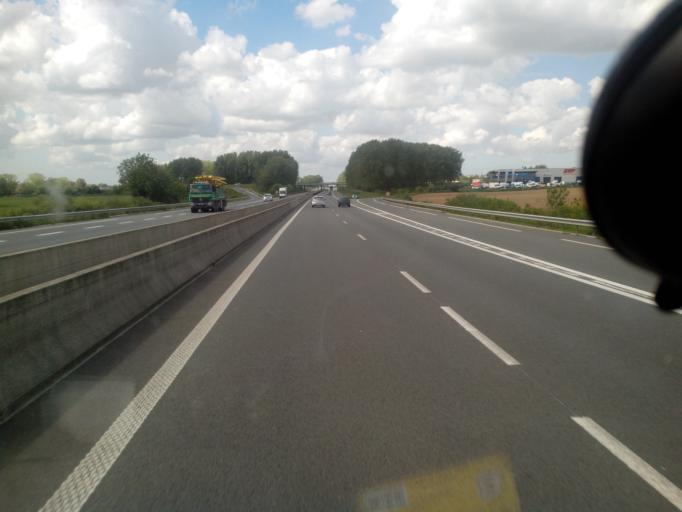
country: FR
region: Nord-Pas-de-Calais
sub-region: Departement du Nord
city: Steenvoorde
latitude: 50.8051
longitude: 2.6017
